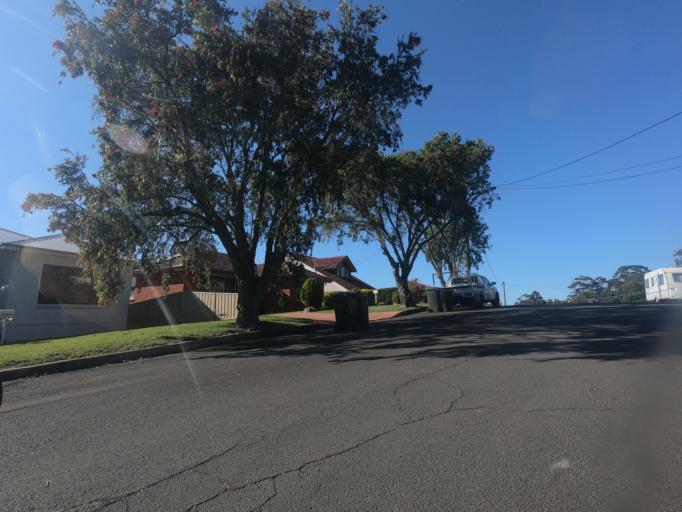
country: AU
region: New South Wales
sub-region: Wollongong
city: Corrimal
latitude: -34.3683
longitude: 150.8913
